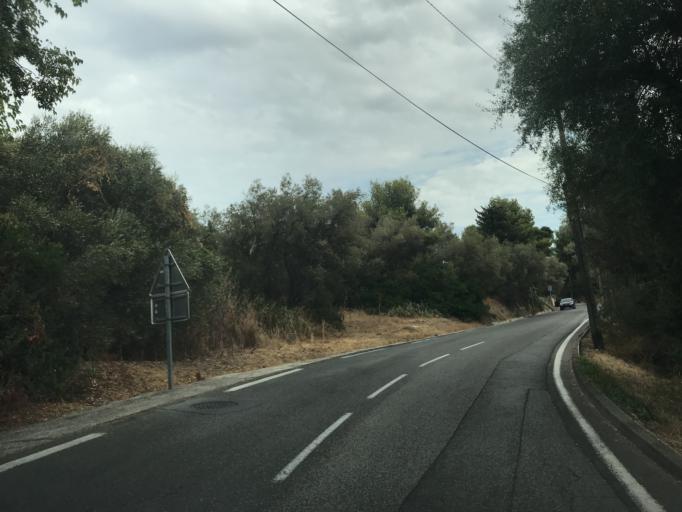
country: FR
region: Provence-Alpes-Cote d'Azur
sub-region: Departement du Var
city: Le Castellet
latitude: 43.1928
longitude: 5.7557
